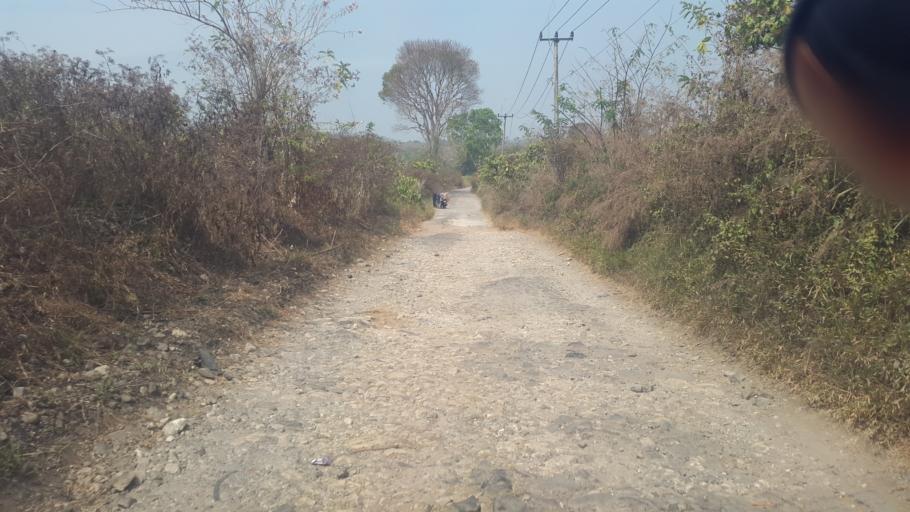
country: ID
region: West Java
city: Ciguna
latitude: -7.0763
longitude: 106.8222
